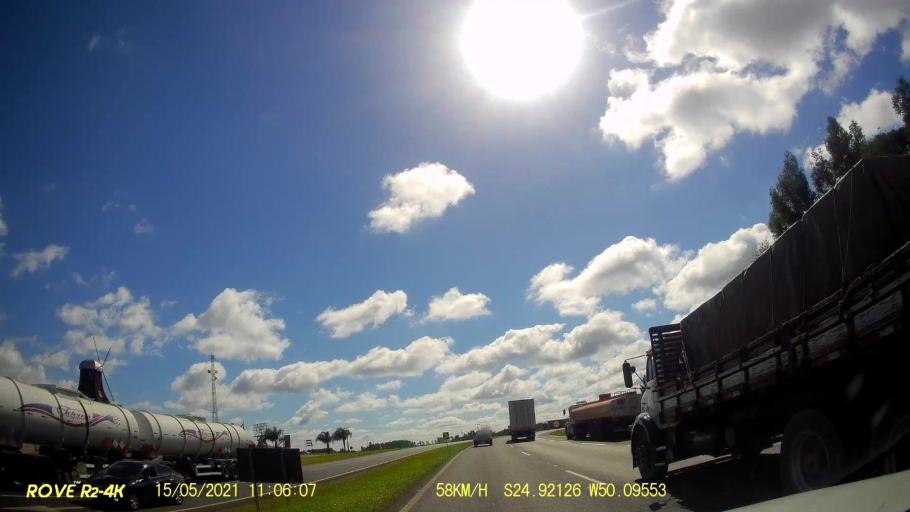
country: BR
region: Parana
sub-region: Carambei
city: Carambei
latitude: -24.9207
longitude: -50.0953
